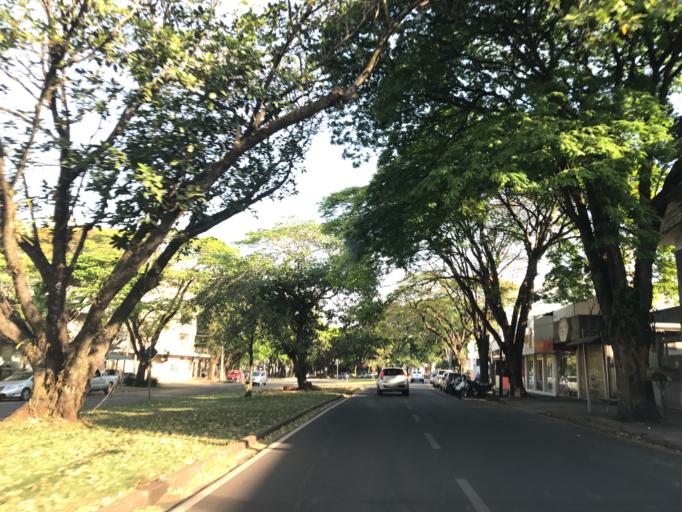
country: BR
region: Parana
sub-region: Maringa
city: Maringa
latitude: -23.4274
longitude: -51.9526
